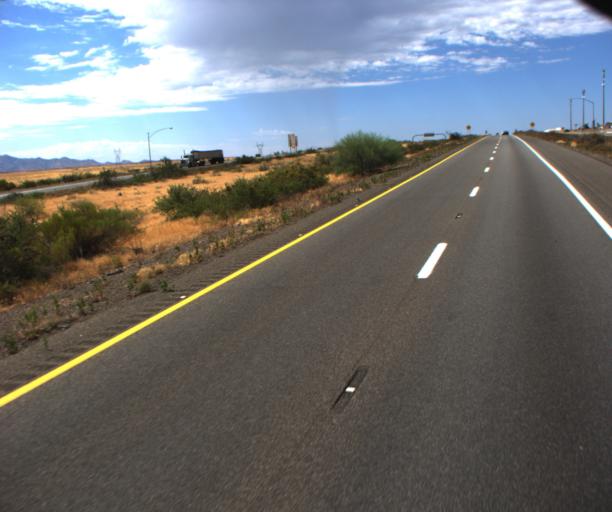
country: US
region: Arizona
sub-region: Yavapai County
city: Black Canyon City
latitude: 34.1900
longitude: -112.1330
